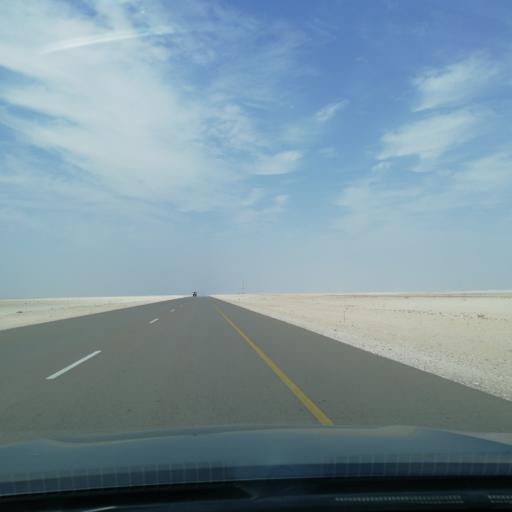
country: OM
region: Al Wusta
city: Hayma'
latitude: 20.2265
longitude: 56.5632
